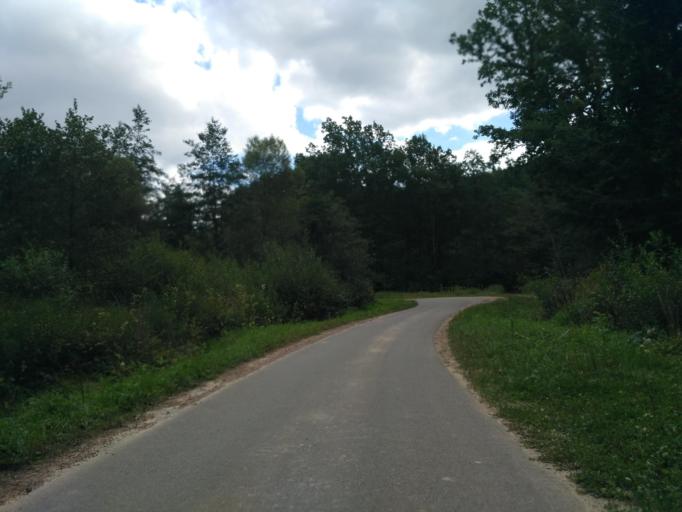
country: PL
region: Subcarpathian Voivodeship
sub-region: Powiat rzeszowski
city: Dynow
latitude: 49.7584
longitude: 22.2852
